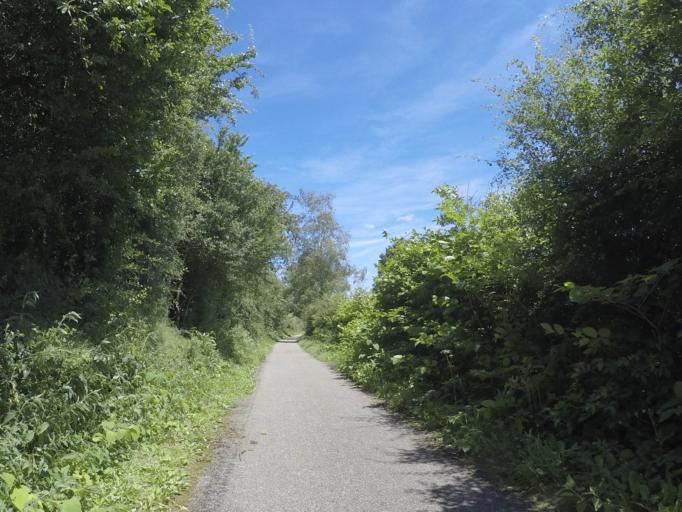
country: BE
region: Wallonia
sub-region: Province de Namur
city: Hamois
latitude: 50.3555
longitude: 5.1786
